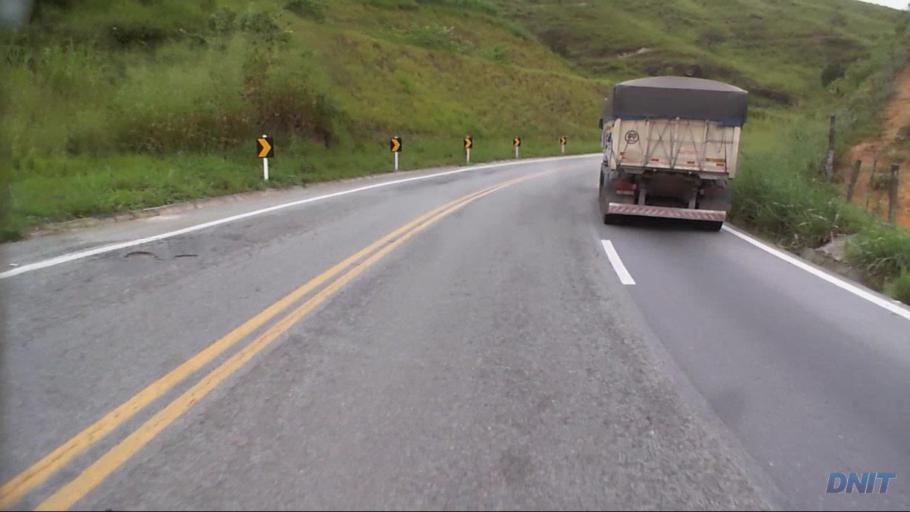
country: BR
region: Minas Gerais
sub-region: Nova Era
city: Nova Era
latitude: -19.6498
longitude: -42.9336
